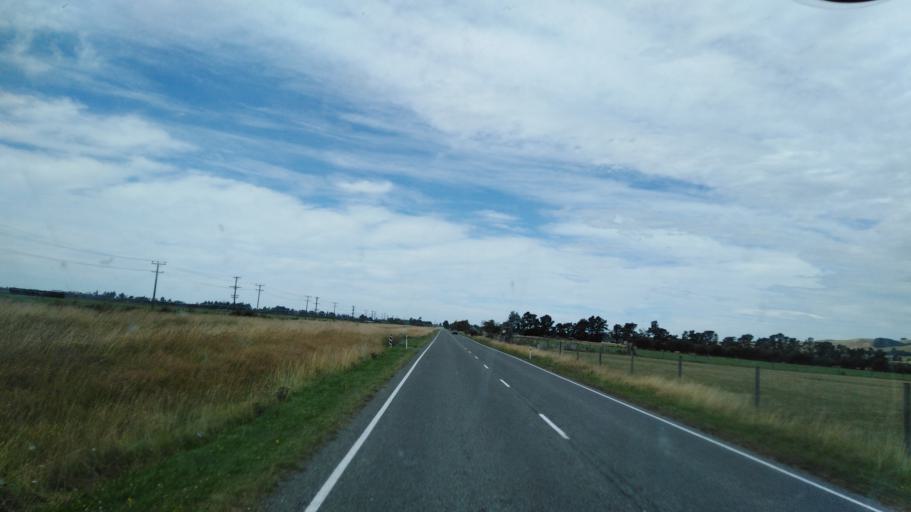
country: NZ
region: Canterbury
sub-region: Selwyn District
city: Darfield
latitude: -43.3616
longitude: 171.9722
